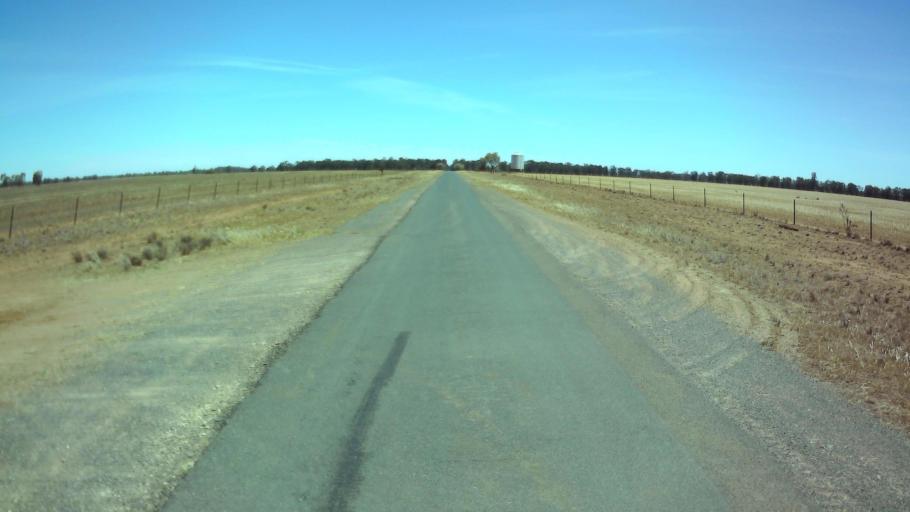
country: AU
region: New South Wales
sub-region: Weddin
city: Grenfell
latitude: -33.8563
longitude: 147.6946
